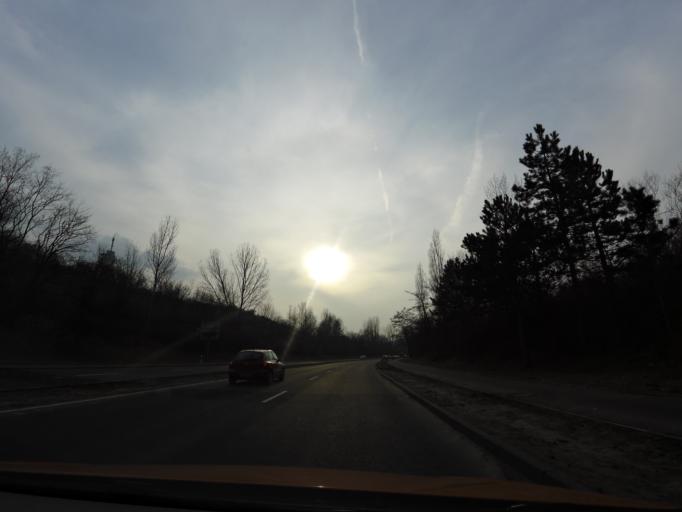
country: DE
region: Brandenburg
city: Frankfurt (Oder)
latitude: 52.3230
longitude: 14.5304
